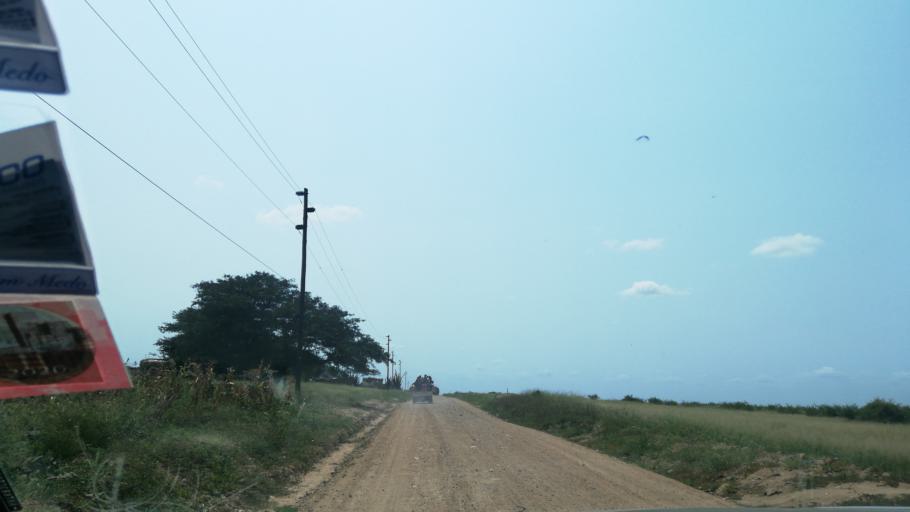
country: MZ
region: Maputo
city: Matola
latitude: -26.0654
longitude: 32.3903
